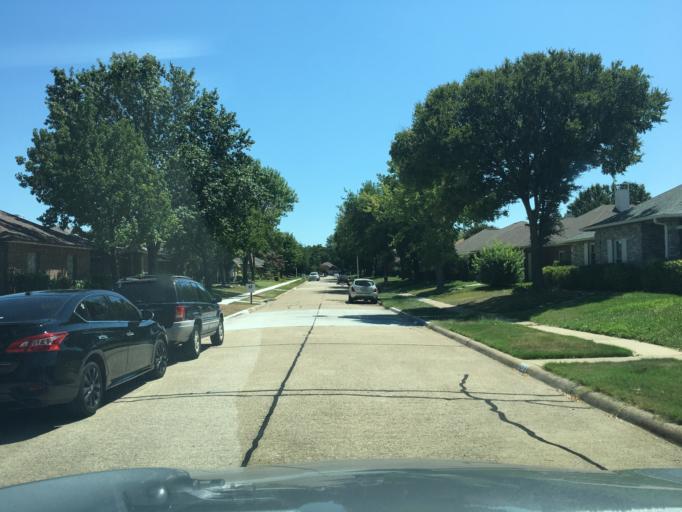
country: US
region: Texas
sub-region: Dallas County
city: Sachse
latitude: 32.9657
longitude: -96.6360
